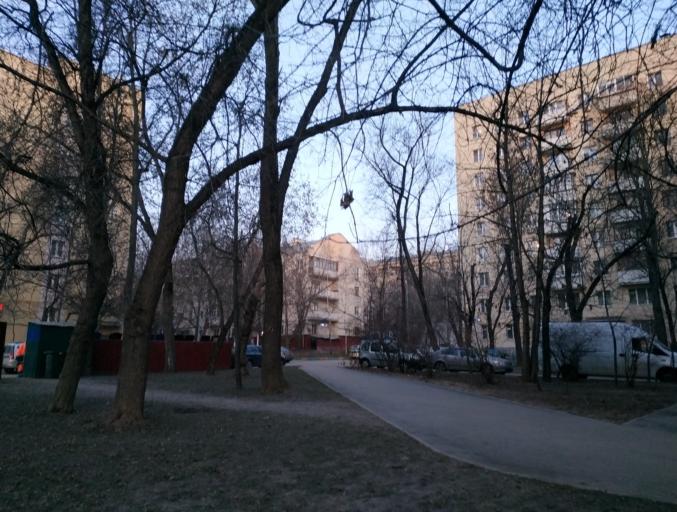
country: RU
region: Moscow
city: Pokrovskoye-Streshnevo
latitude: 55.8314
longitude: 37.4474
